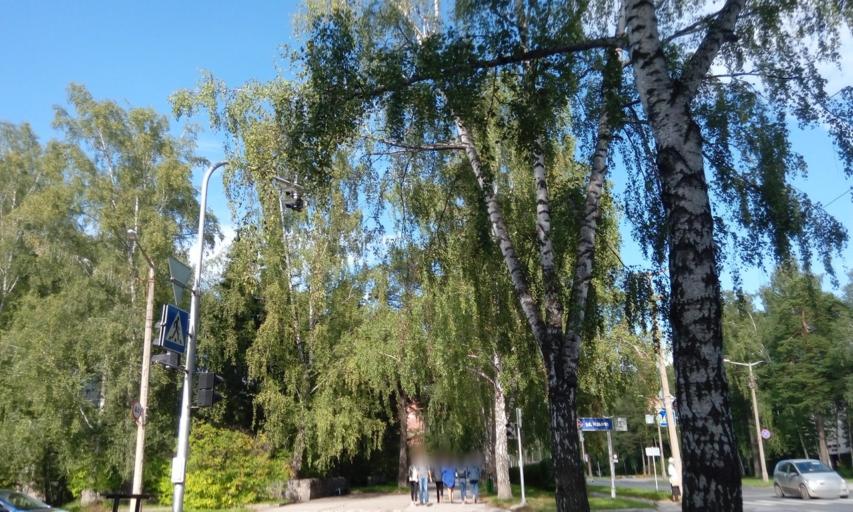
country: RU
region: Novosibirsk
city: Akademgorodok
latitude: 54.8362
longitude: 83.0997
